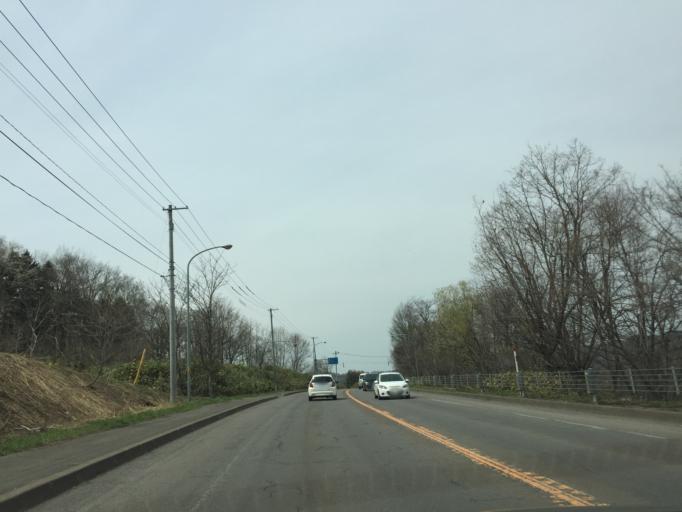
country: JP
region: Hokkaido
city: Ashibetsu
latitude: 43.5354
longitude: 142.1452
